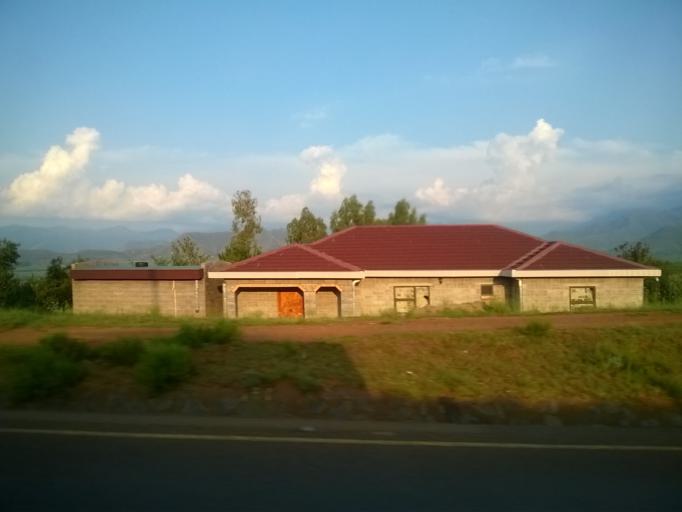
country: LS
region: Leribe
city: Leribe
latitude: -29.0154
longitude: 28.2183
